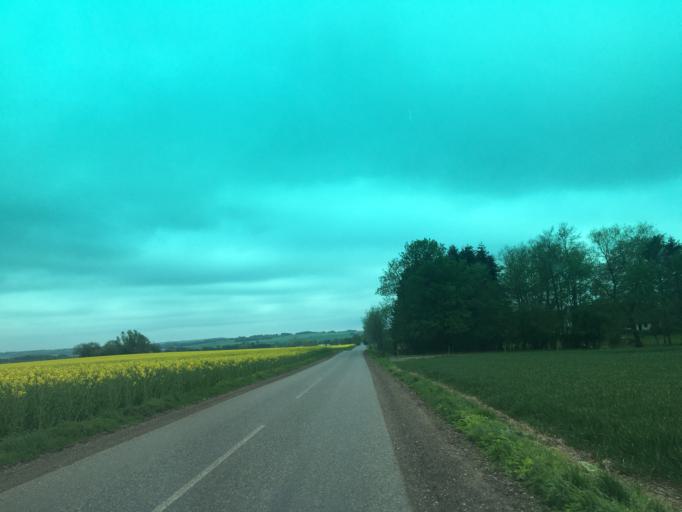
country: DK
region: Zealand
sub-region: Ringsted Kommune
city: Ringsted
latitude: 55.4254
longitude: 11.7117
